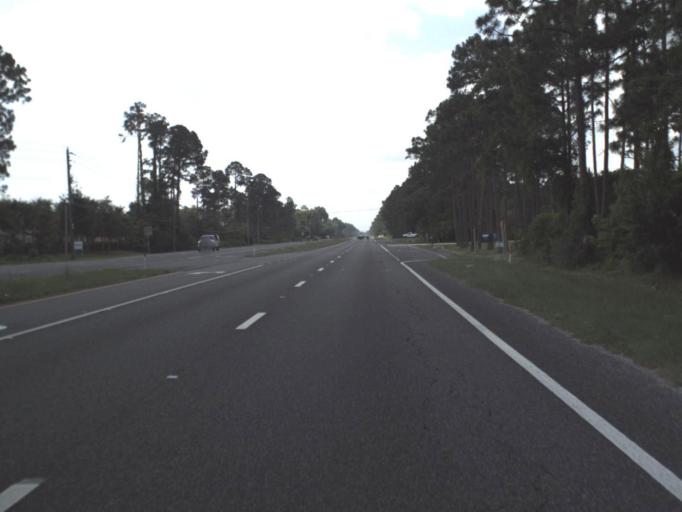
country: US
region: Florida
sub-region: Saint Johns County
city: Saint Augustine Shores
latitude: 29.7863
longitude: -81.3181
